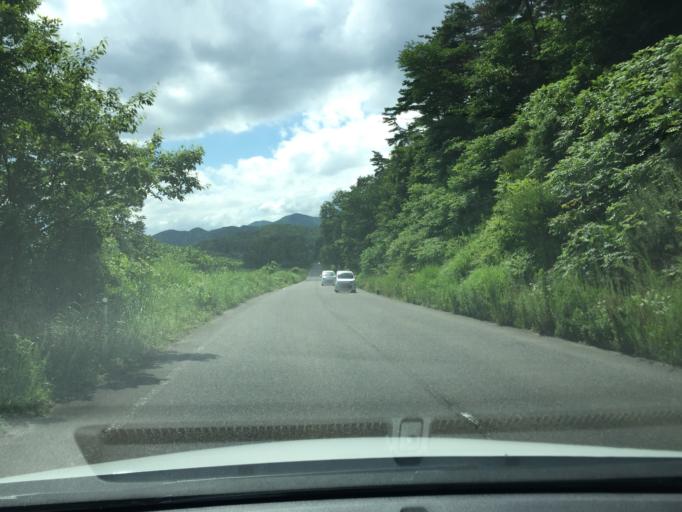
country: JP
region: Fukushima
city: Koriyama
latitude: 37.3445
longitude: 140.2532
